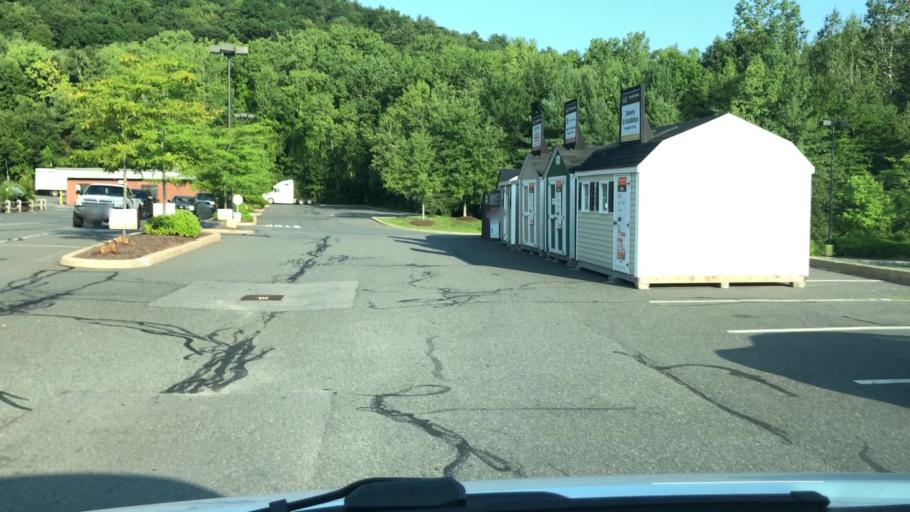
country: US
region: Massachusetts
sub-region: Franklin County
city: Greenfield
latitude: 42.5859
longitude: -72.6277
